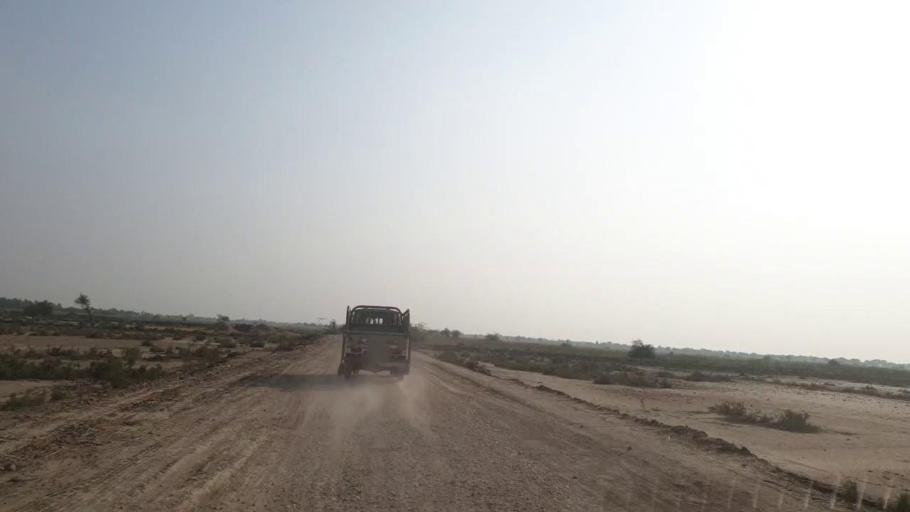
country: PK
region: Sindh
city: Kario
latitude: 24.9108
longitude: 68.5687
